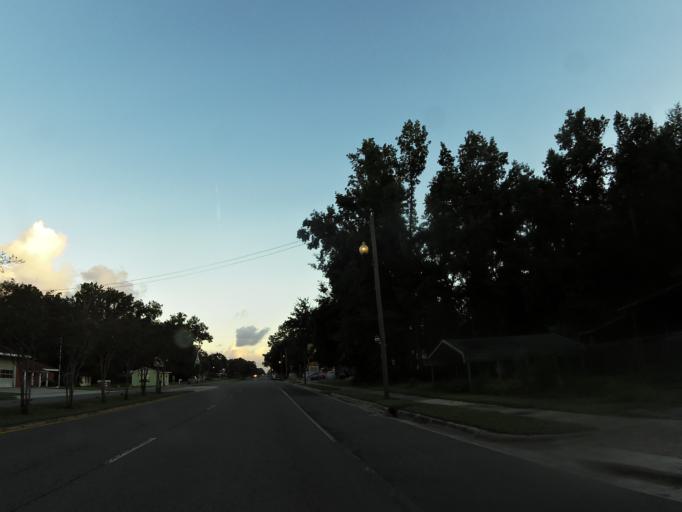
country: US
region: Georgia
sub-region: Camden County
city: Woodbine
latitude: 30.9649
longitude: -81.7231
